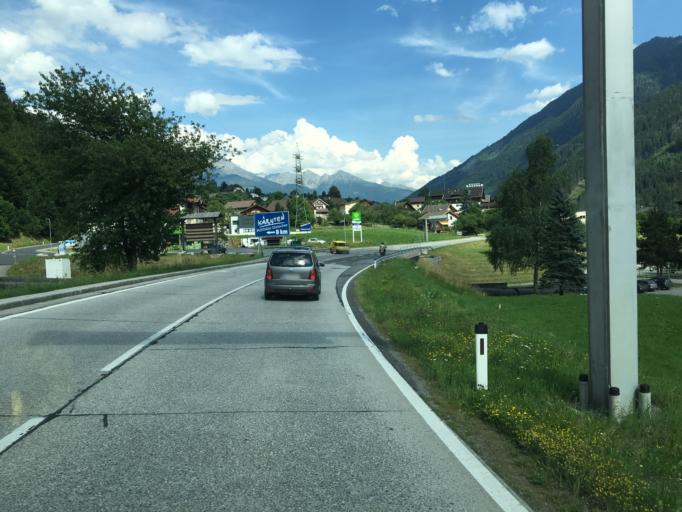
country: AT
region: Carinthia
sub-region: Politischer Bezirk Spittal an der Drau
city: Flattach
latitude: 46.9355
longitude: 13.1088
